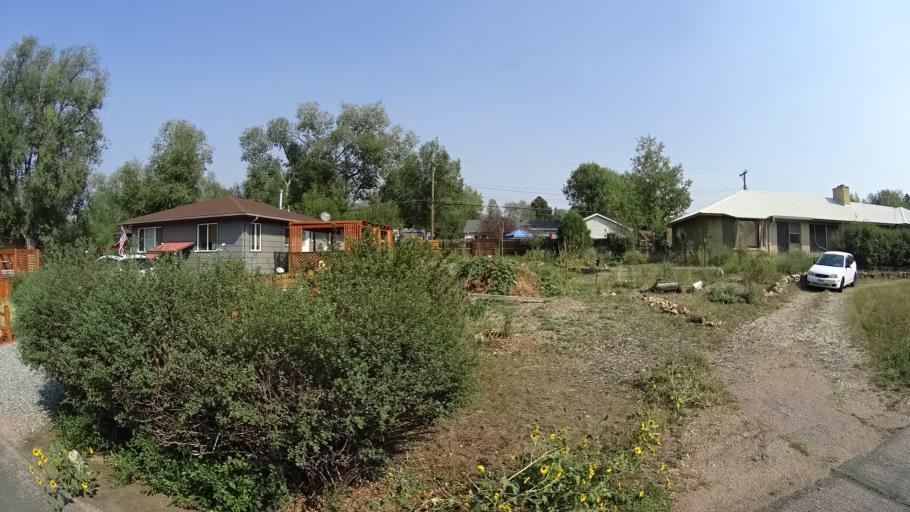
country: US
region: Colorado
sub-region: El Paso County
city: Colorado Springs
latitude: 38.8121
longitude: -104.8384
